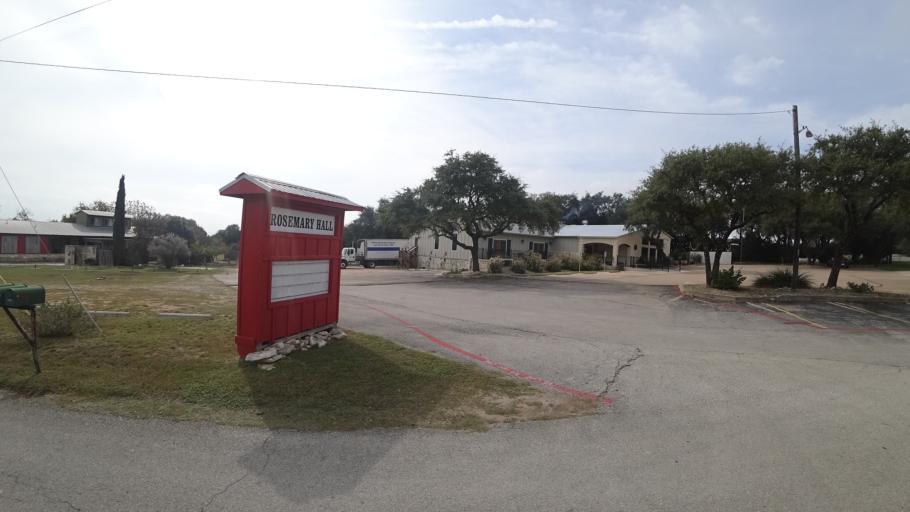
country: US
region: Texas
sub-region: Travis County
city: Hudson Bend
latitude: 30.3968
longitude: -97.9311
